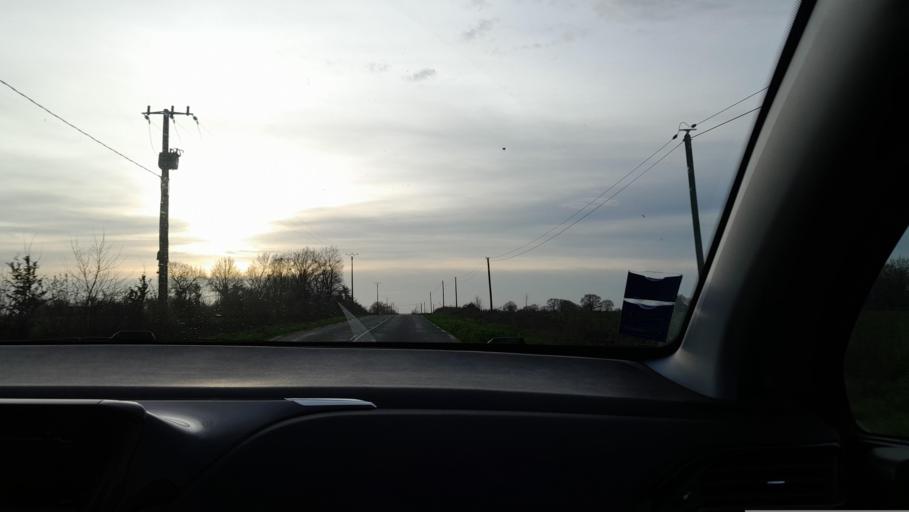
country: FR
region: Pays de la Loire
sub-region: Departement de la Mayenne
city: Ballots
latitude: 47.9332
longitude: -1.0778
